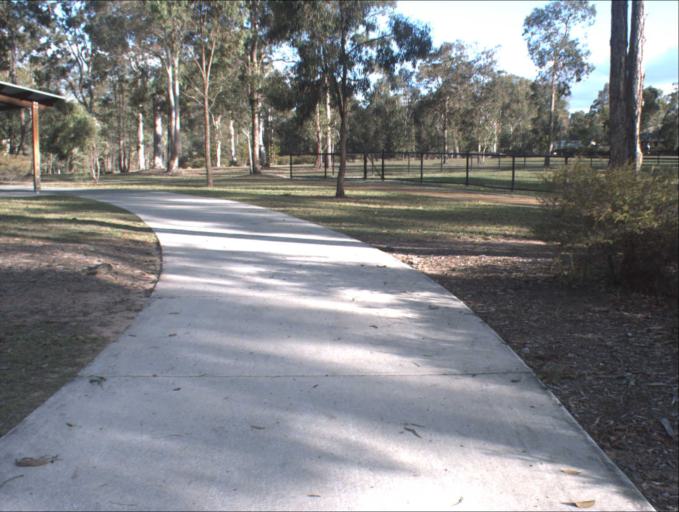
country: AU
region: Queensland
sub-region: Logan
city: North Maclean
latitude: -27.7539
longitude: 152.9677
